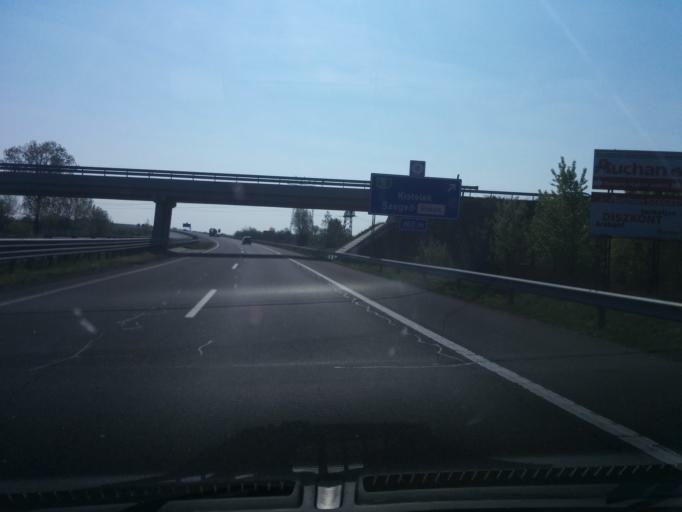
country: HU
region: Csongrad
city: Szatymaz
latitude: 46.2951
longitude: 20.0673
